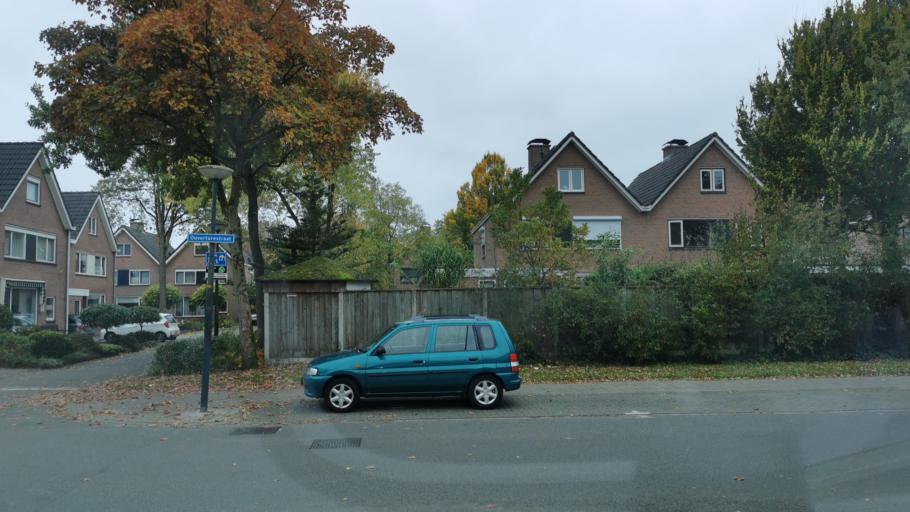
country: DE
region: North Rhine-Westphalia
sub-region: Regierungsbezirk Munster
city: Gronau
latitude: 52.2093
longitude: 6.9698
